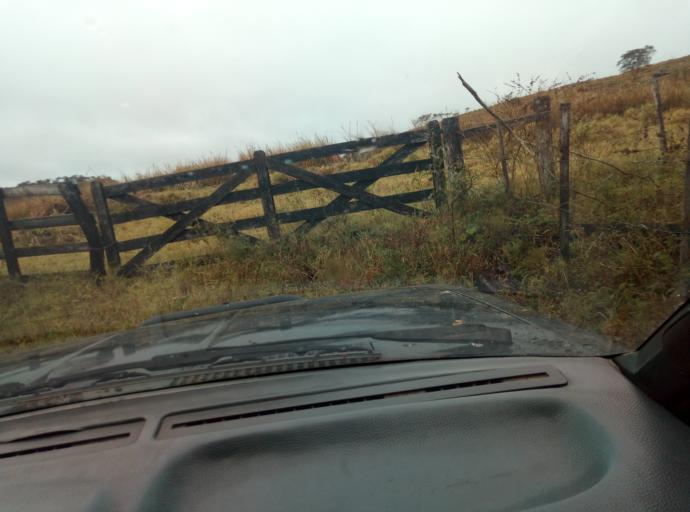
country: PY
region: Caaguazu
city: Carayao
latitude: -25.1981
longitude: -56.3544
